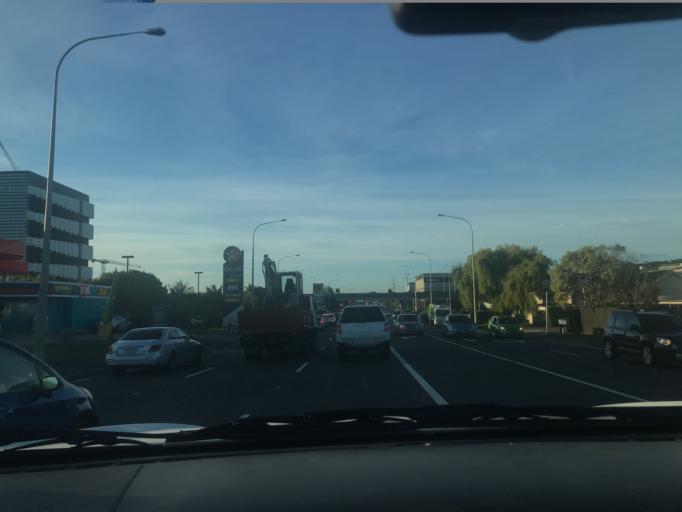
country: NZ
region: Auckland
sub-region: Auckland
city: Tamaki
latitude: -36.9136
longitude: 174.8386
